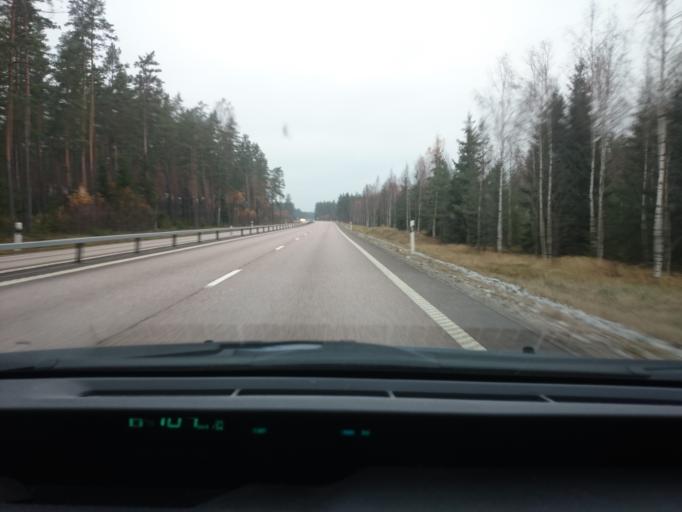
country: SE
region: Dalarna
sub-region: Avesta Kommun
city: Avesta
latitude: 60.0535
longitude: 16.3383
